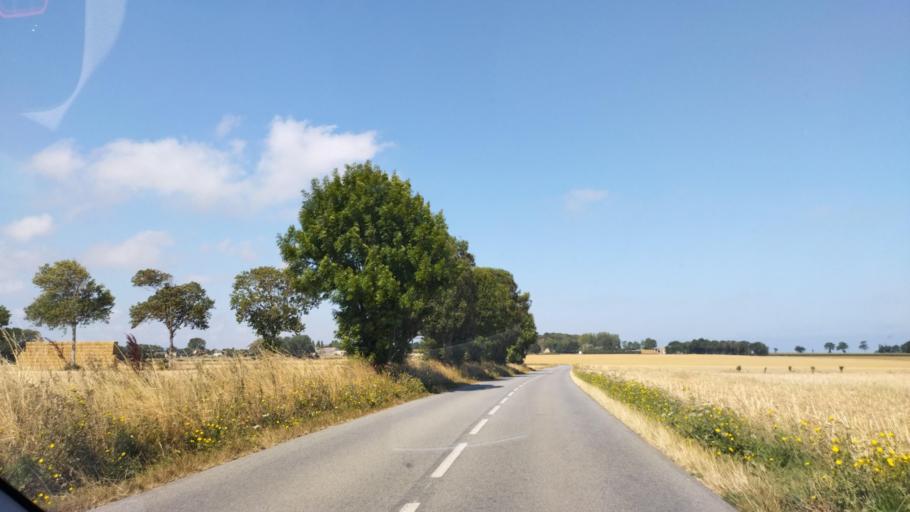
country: FR
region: Lower Normandy
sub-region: Departement du Calvados
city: Douvres-la-Delivrande
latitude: 49.3036
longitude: -0.3974
